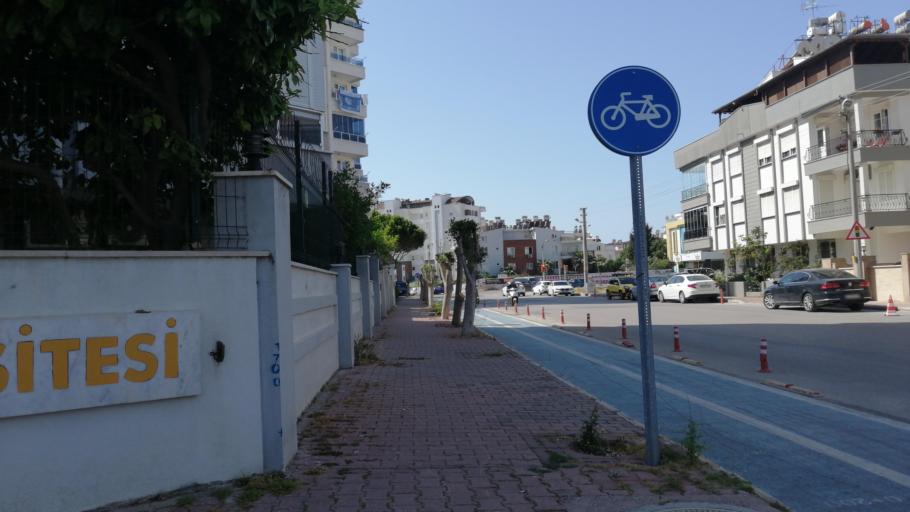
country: TR
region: Antalya
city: Antalya
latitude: 36.8574
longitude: 30.7836
